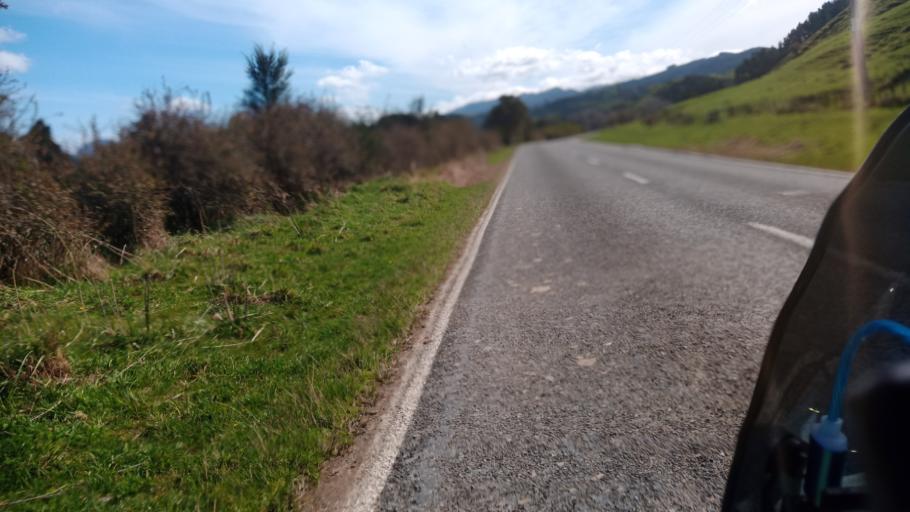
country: NZ
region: Gisborne
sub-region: Gisborne District
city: Gisborne
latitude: -37.8723
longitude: 178.2768
